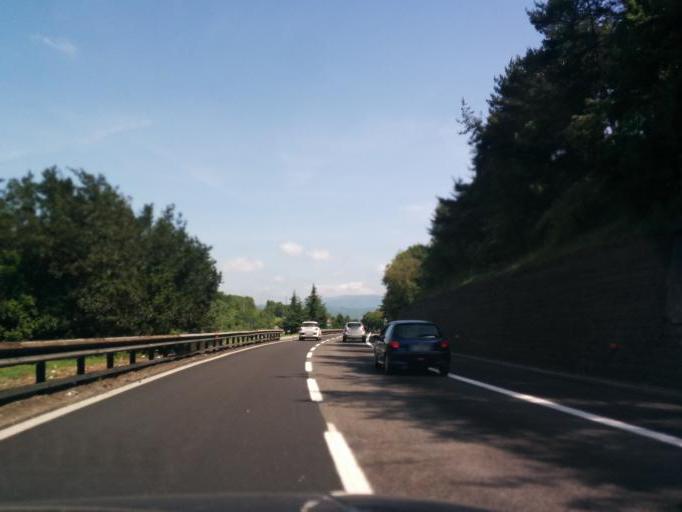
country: IT
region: Tuscany
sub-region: Province of Florence
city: Cavallina
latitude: 43.9405
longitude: 11.2216
